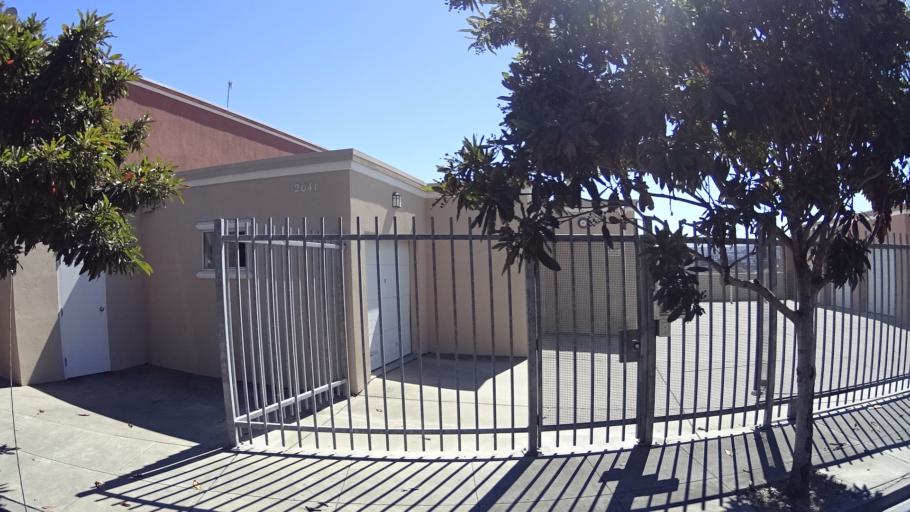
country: US
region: California
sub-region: San Francisco County
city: San Francisco
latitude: 37.7508
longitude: -122.4001
